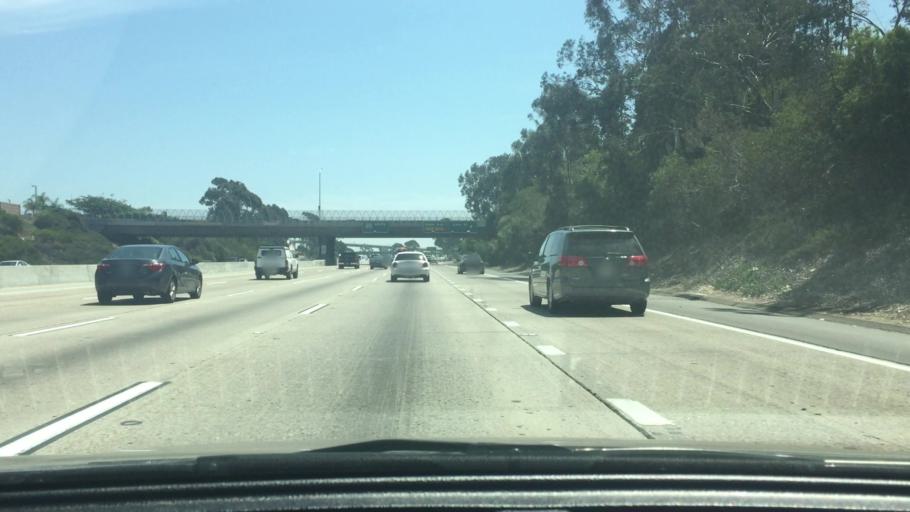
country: US
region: California
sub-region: San Diego County
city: National City
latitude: 32.6984
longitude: -117.0951
